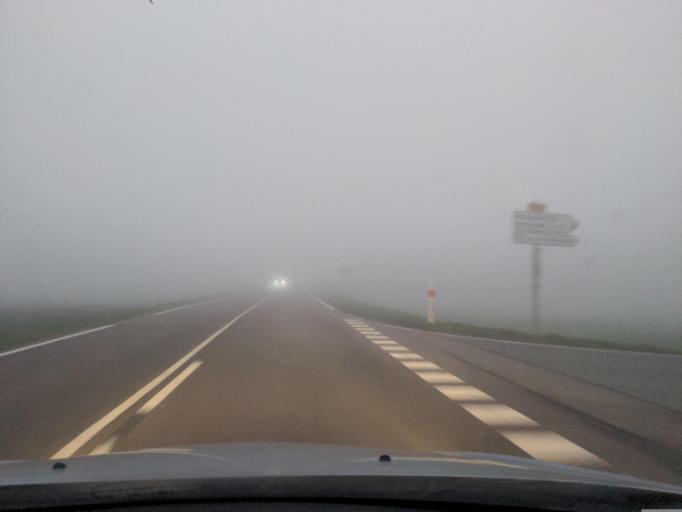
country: FR
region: Champagne-Ardenne
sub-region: Departement de la Haute-Marne
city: Langres
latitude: 47.8030
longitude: 5.2553
